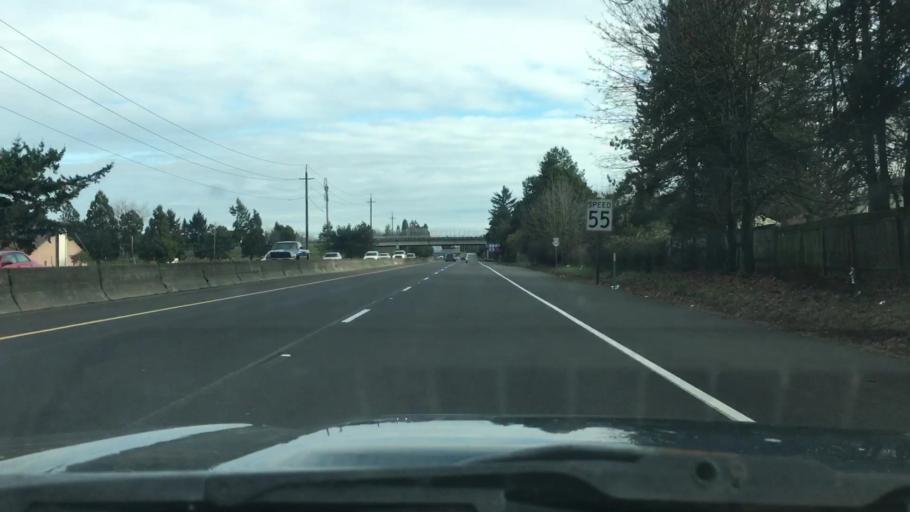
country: US
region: Oregon
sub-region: Lane County
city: Eugene
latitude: 44.0895
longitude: -123.0916
